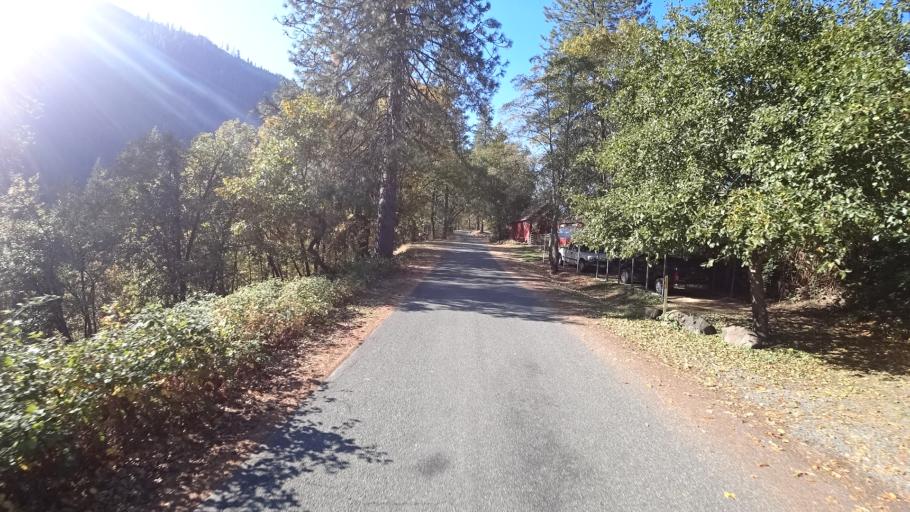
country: US
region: California
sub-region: Siskiyou County
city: Happy Camp
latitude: 41.6927
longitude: -123.0672
